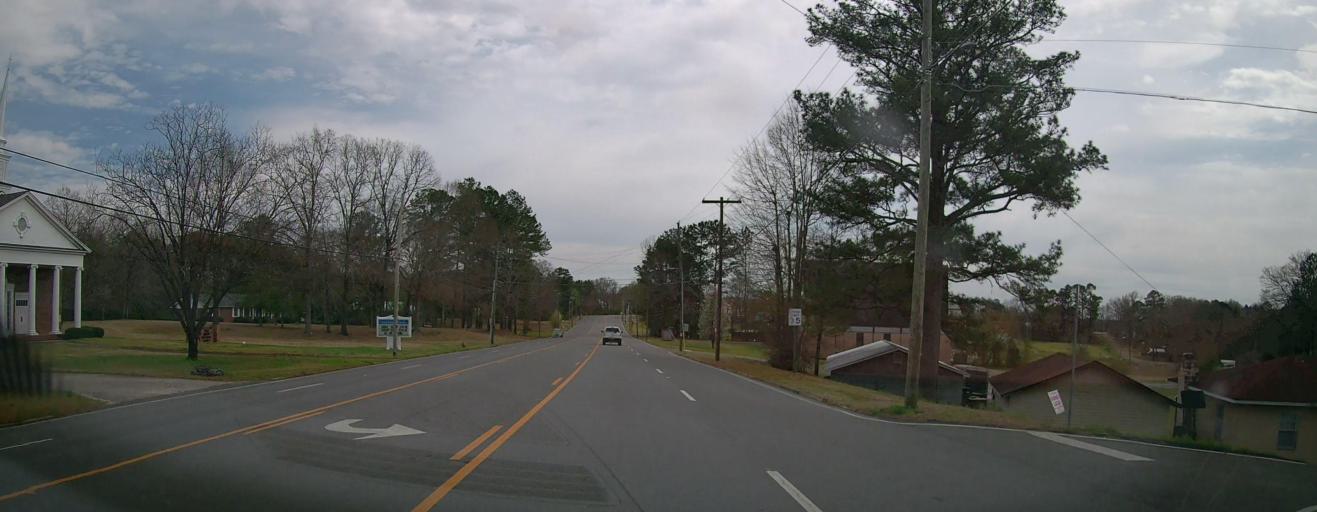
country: US
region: Alabama
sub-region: Marion County
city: Guin
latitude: 33.9778
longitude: -87.9171
